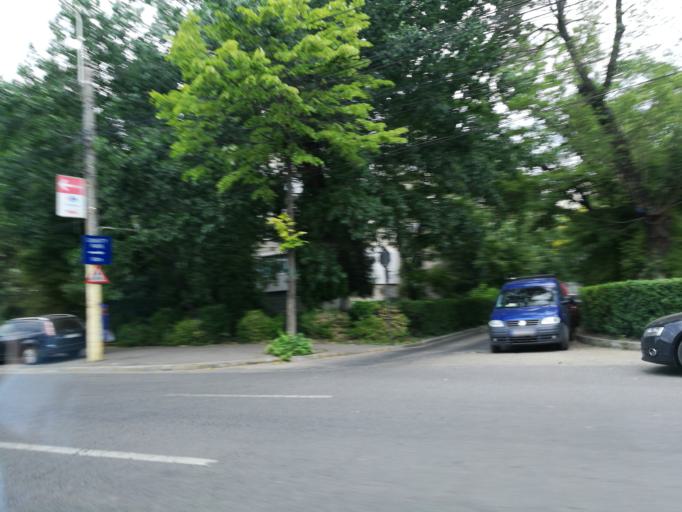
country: RO
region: Constanta
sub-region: Municipiul Constanta
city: Constanta
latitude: 44.2013
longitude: 28.6308
